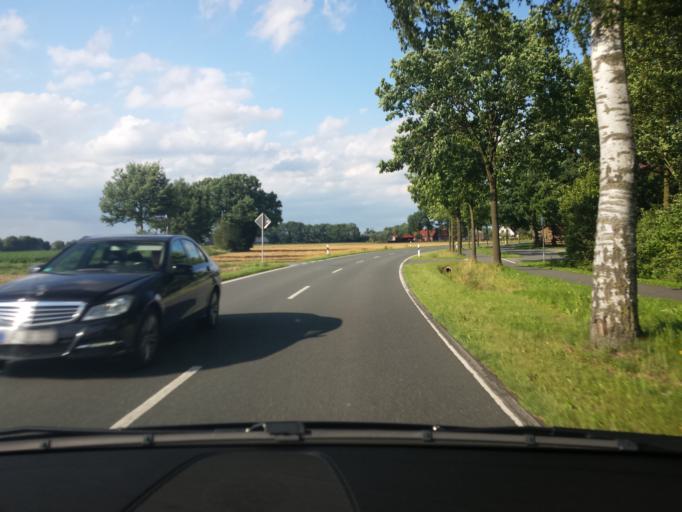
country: DE
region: North Rhine-Westphalia
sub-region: Regierungsbezirk Arnsberg
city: Lippstadt
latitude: 51.6903
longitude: 8.3003
